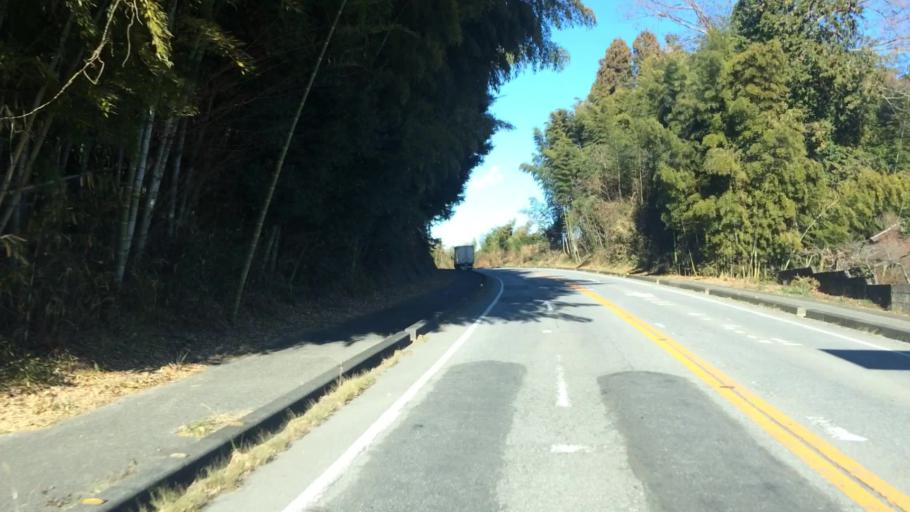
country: JP
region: Tochigi
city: Utsunomiya-shi
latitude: 36.6408
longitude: 139.8347
